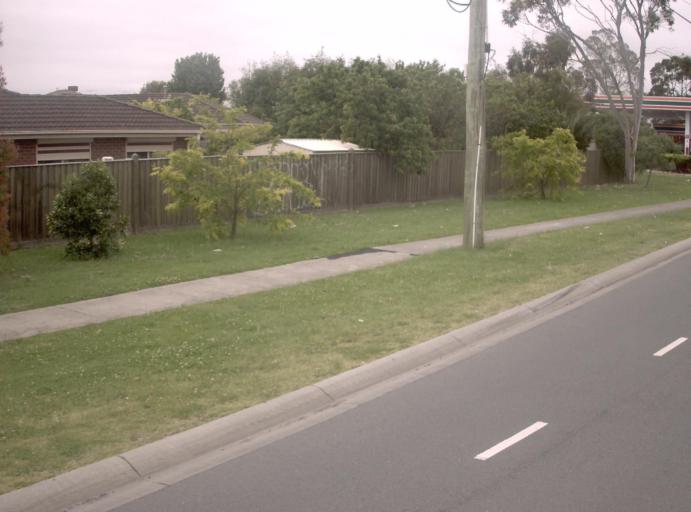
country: AU
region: Victoria
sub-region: Casey
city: Hallam
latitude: -38.0031
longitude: 145.2739
